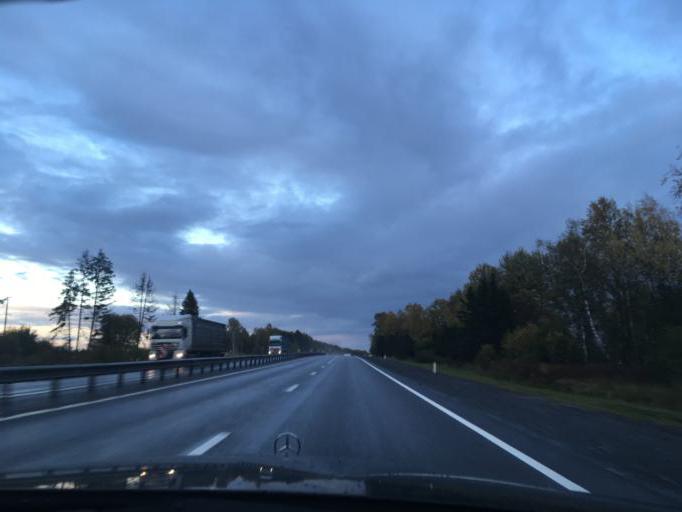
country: RU
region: Smolensk
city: Yartsevo
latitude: 55.1043
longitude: 32.9255
